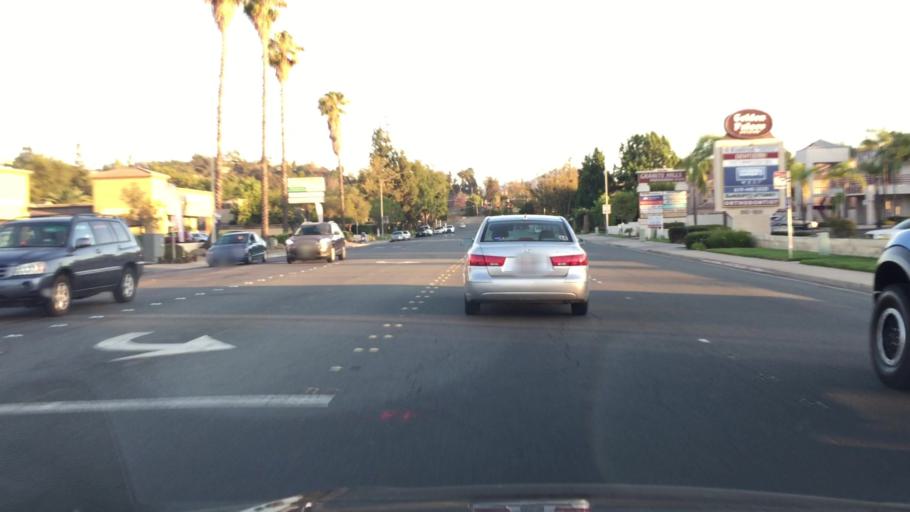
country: US
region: California
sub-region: San Diego County
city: Bostonia
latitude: 32.7852
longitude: -116.9280
